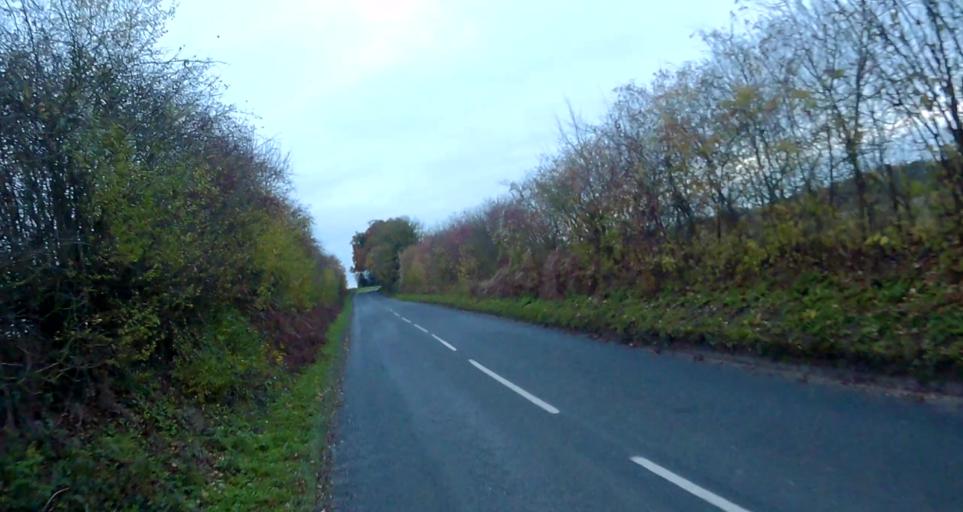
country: GB
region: England
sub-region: Hampshire
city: Odiham
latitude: 51.2432
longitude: -0.9757
